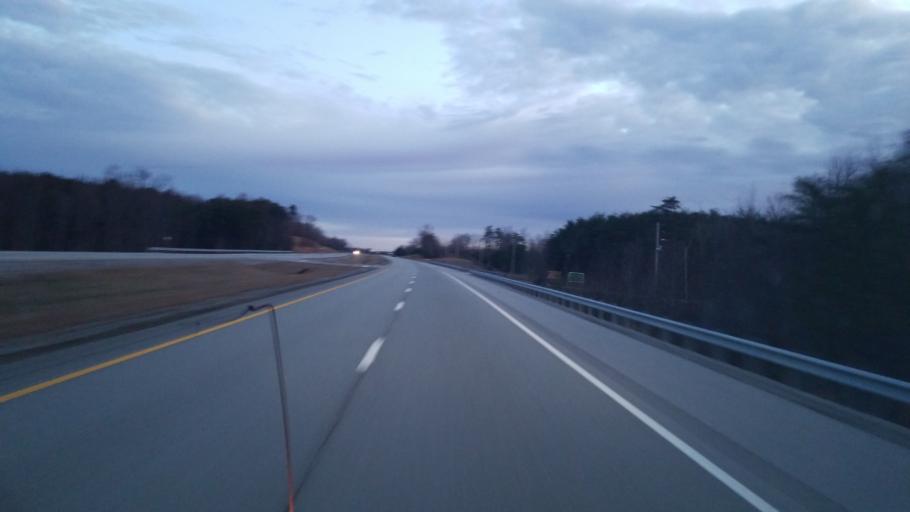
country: US
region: Tennessee
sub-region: Van Buren County
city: Spencer
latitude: 35.7044
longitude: -85.4768
